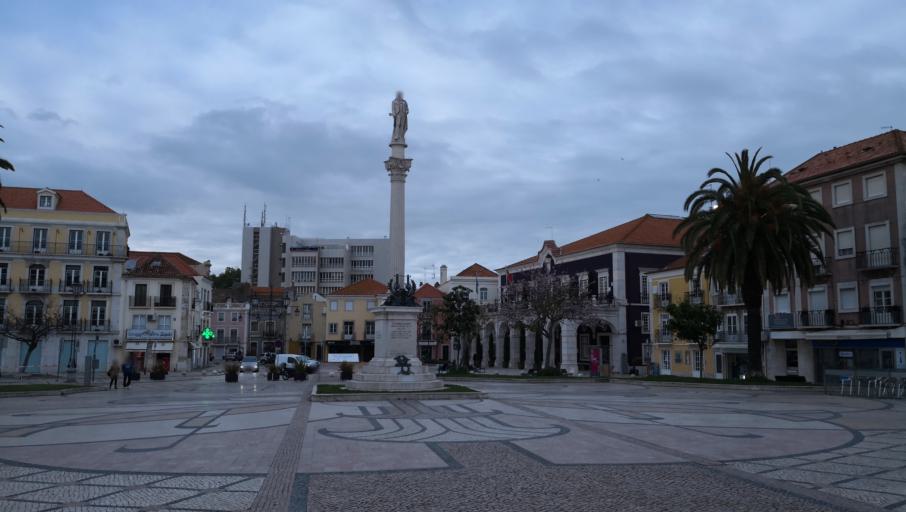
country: PT
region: Setubal
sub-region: Setubal
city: Setubal
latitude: 38.5241
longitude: -8.8926
